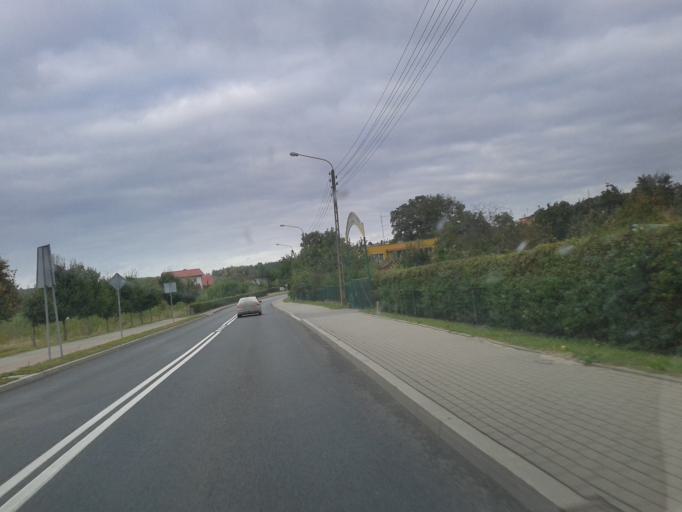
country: PL
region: Kujawsko-Pomorskie
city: Kamien Krajenski
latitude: 53.5314
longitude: 17.5138
